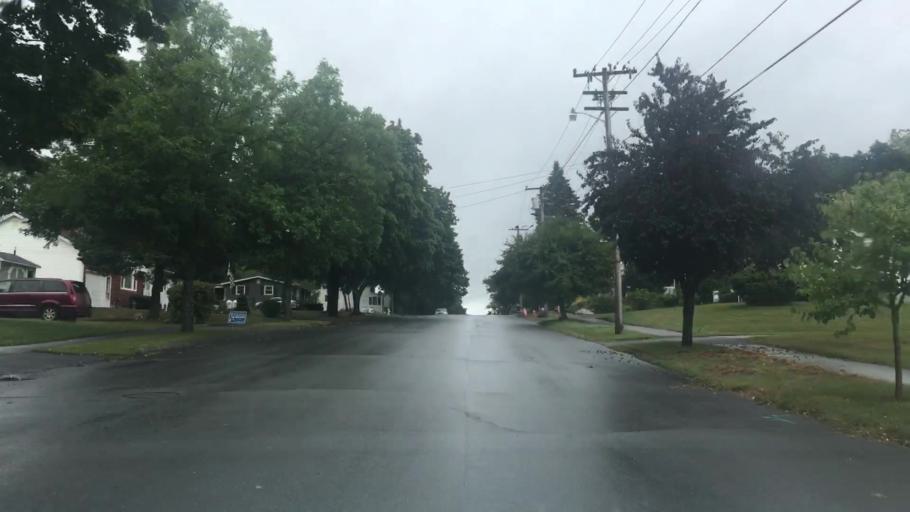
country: US
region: Maine
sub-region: Penobscot County
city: Brewer
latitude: 44.8185
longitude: -68.7608
